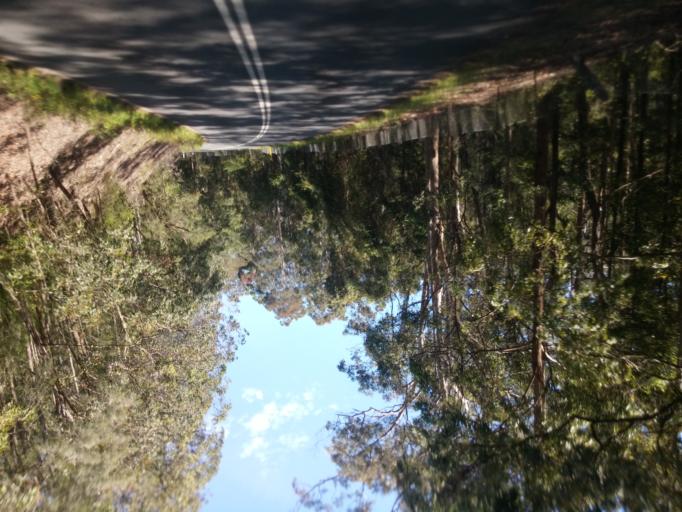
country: AU
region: New South Wales
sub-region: Great Lakes
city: Bulahdelah
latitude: -32.4038
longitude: 152.2968
